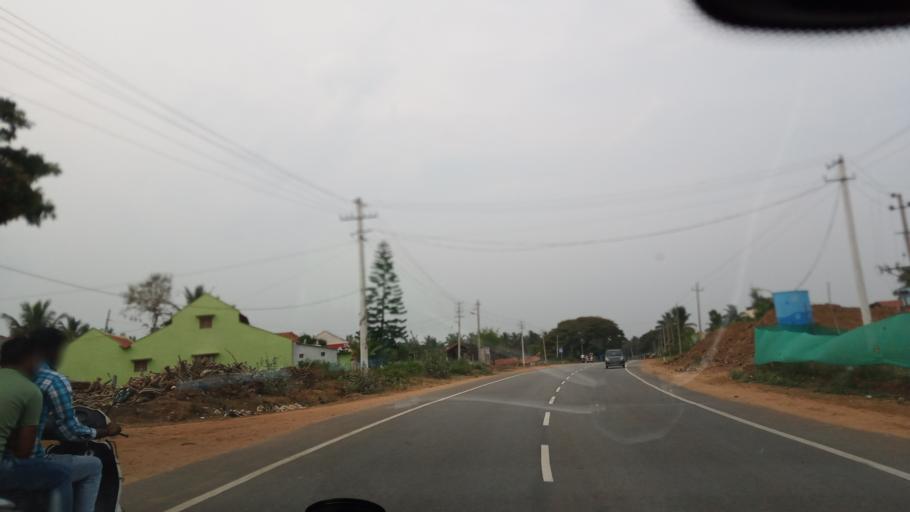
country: IN
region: Karnataka
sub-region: Mandya
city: Nagamangala
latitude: 12.7330
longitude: 76.7184
